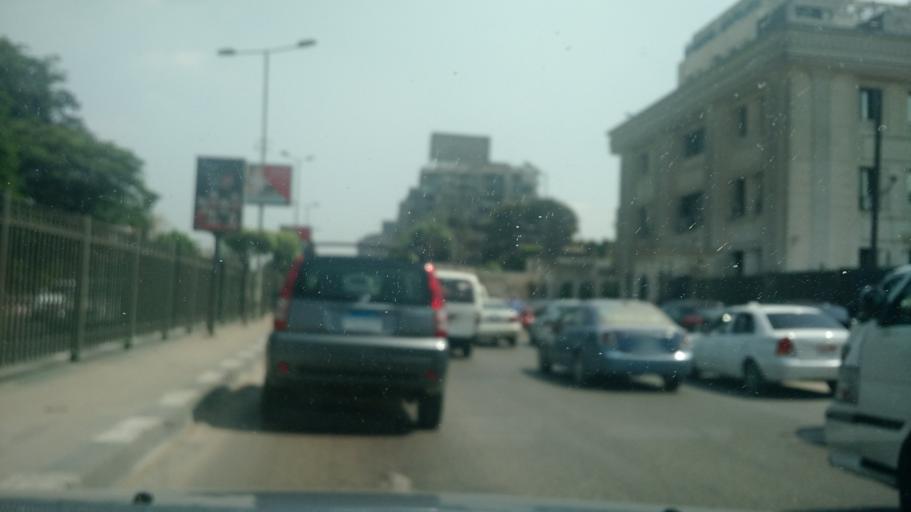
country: EG
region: Al Jizah
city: Al Jizah
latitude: 30.0119
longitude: 31.2280
